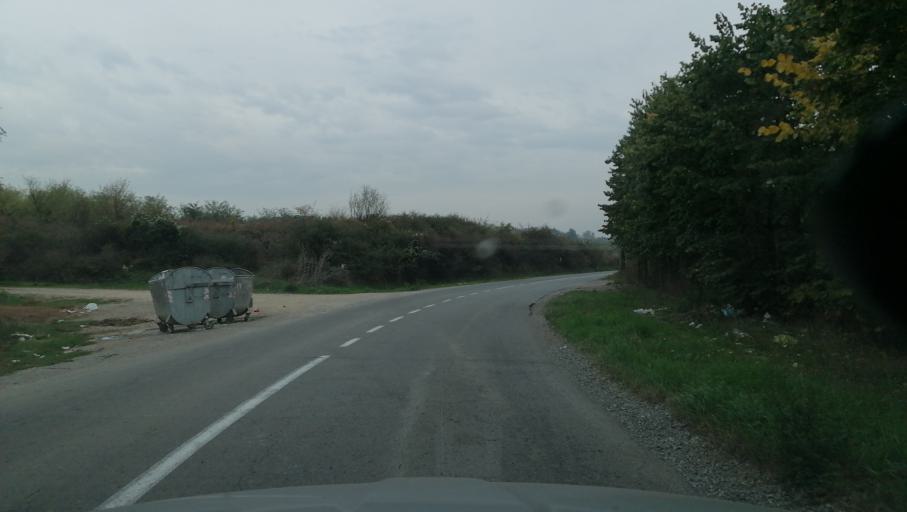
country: RS
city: Rusanj
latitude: 44.6789
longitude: 20.5061
